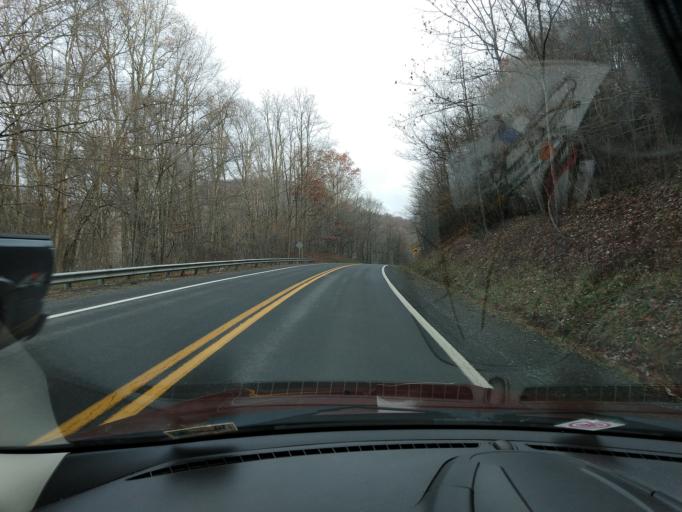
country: US
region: West Virginia
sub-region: Greenbrier County
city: Rainelle
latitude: 38.0381
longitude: -80.7294
